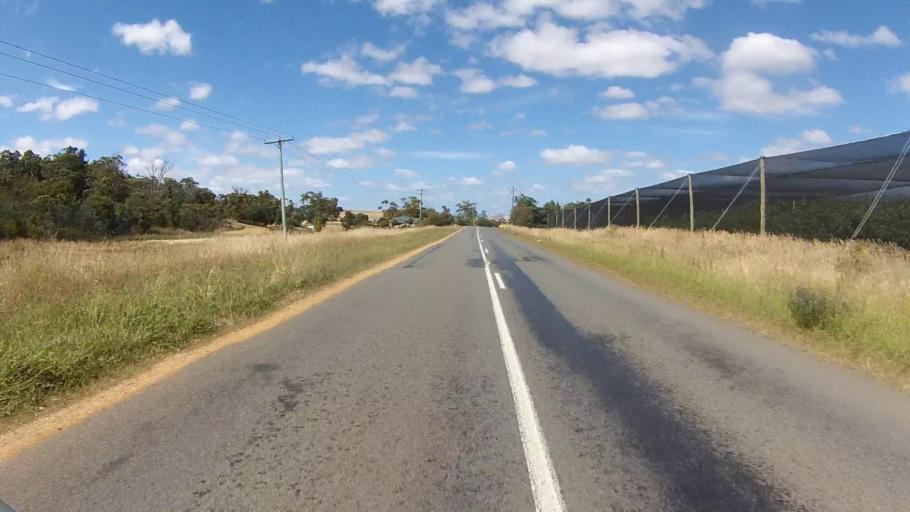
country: AU
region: Tasmania
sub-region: Sorell
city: Sorell
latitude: -42.6482
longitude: 147.4340
